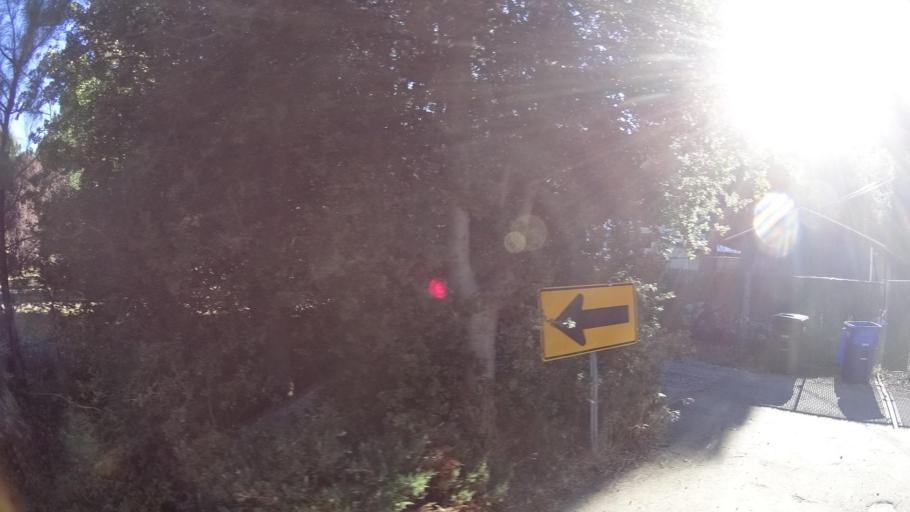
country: US
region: California
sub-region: San Diego County
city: Pine Valley
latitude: 32.8233
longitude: -116.5204
